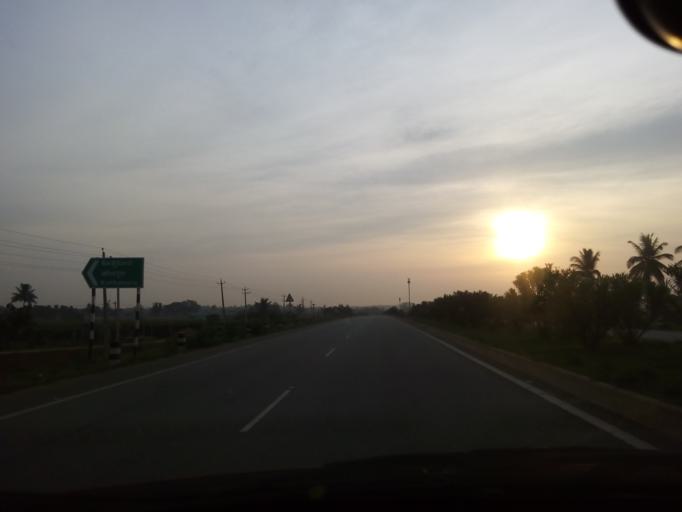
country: IN
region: Karnataka
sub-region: Chikkaballapur
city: Chik Ballapur
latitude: 13.3891
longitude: 77.7349
